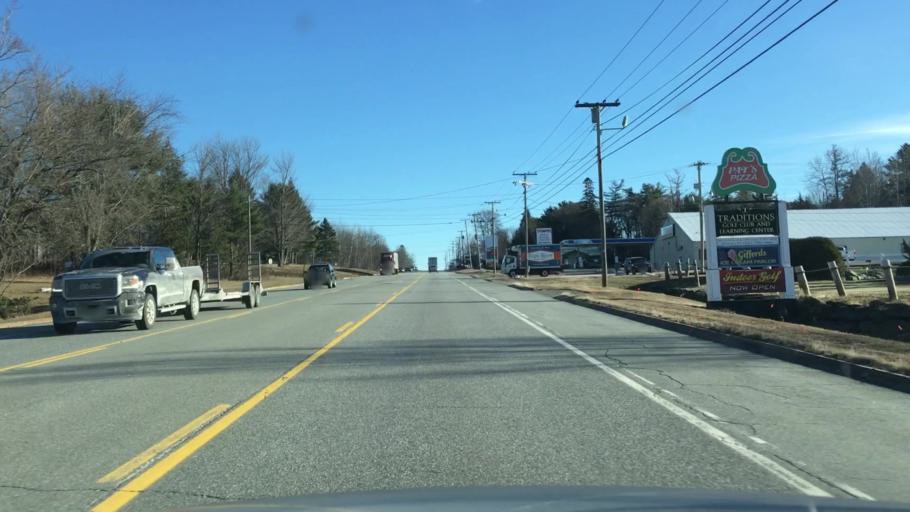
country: US
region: Maine
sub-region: Penobscot County
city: Holden
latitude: 44.7673
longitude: -68.7122
